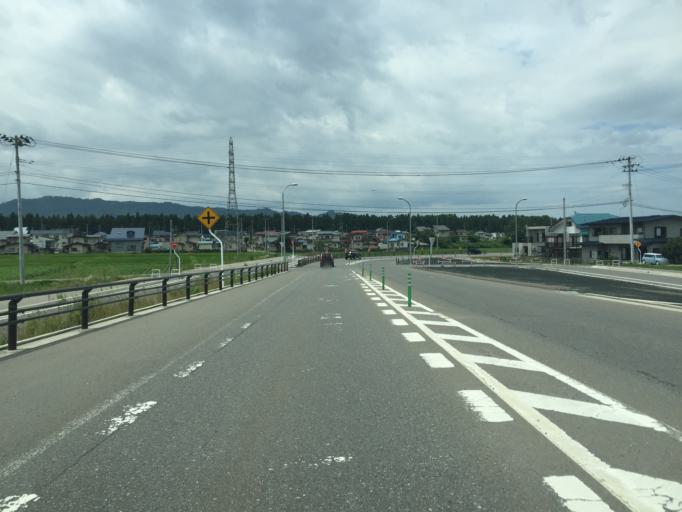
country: JP
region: Yamagata
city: Yonezawa
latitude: 37.8991
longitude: 140.1371
